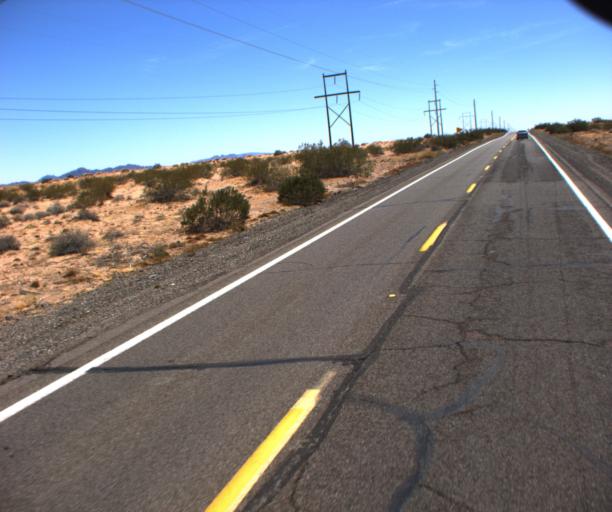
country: US
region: Arizona
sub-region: La Paz County
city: Parker
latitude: 33.9498
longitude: -114.2169
